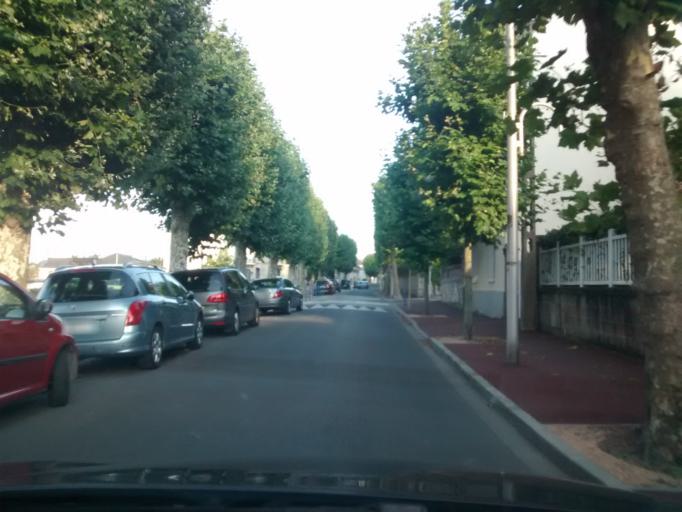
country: FR
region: Lower Normandy
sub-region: Departement du Calvados
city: Villers-sur-Mer
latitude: 49.3211
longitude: -0.0019
